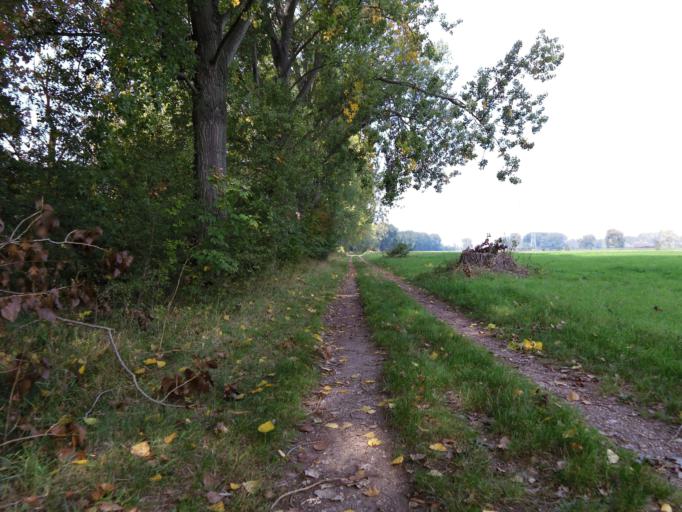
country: DE
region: Rheinland-Pfalz
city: Worms
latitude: 49.6632
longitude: 8.3692
